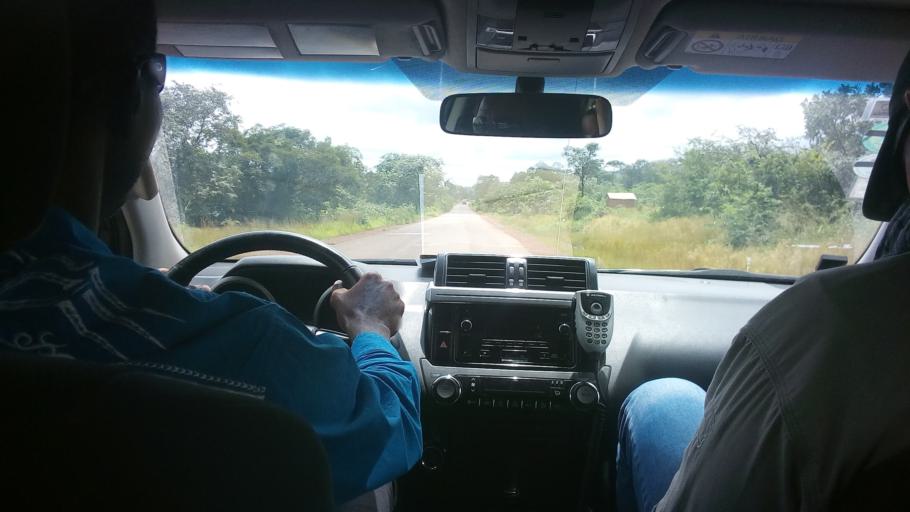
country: GN
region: Boke
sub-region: Boke Prefecture
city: Boke
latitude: 11.0227
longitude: -14.0653
